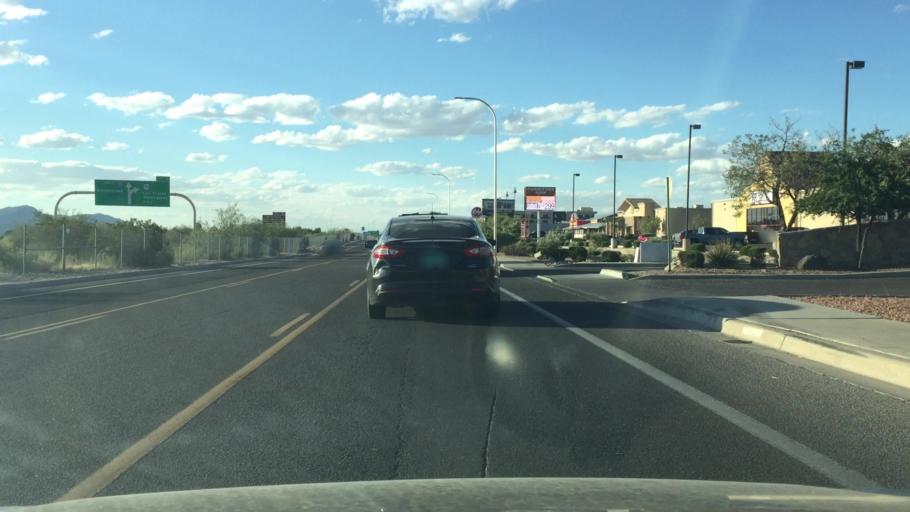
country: US
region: New Mexico
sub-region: Dona Ana County
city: Las Cruces
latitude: 32.3319
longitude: -106.7578
